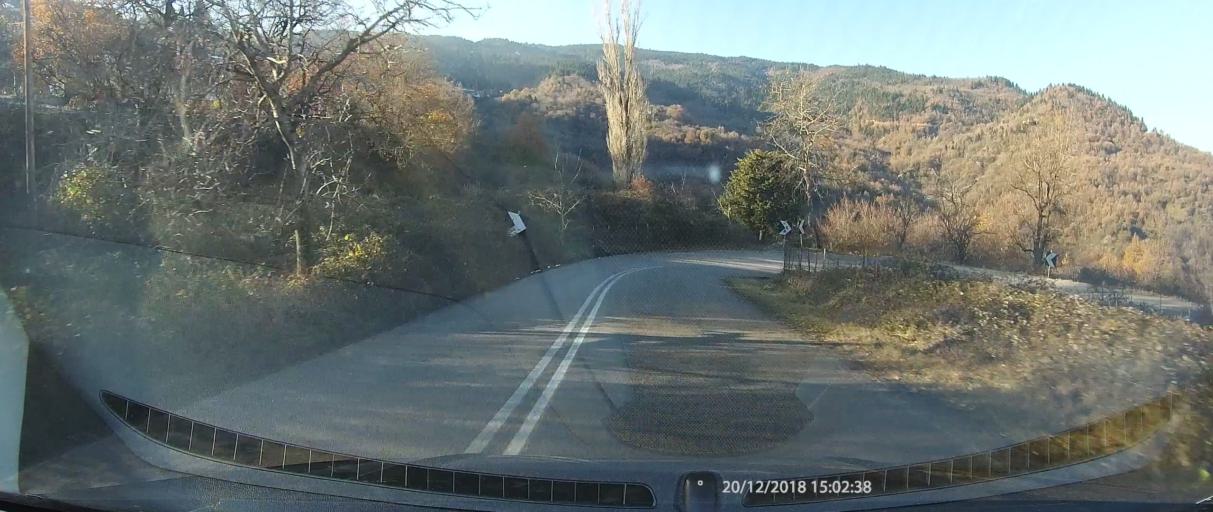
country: GR
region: Central Greece
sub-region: Nomos Evrytanias
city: Karpenisi
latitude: 38.9119
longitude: 21.9200
